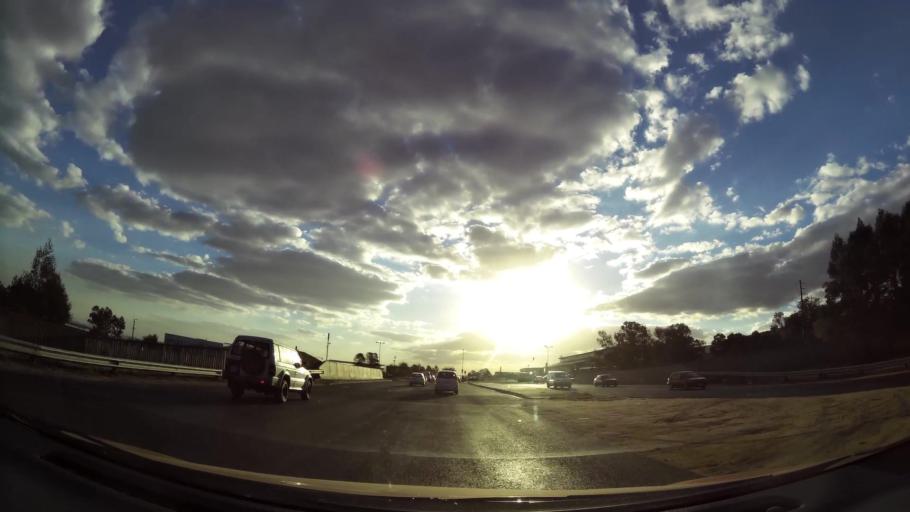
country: ZA
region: Gauteng
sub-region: City of Johannesburg Metropolitan Municipality
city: Midrand
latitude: -25.9436
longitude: 28.1452
